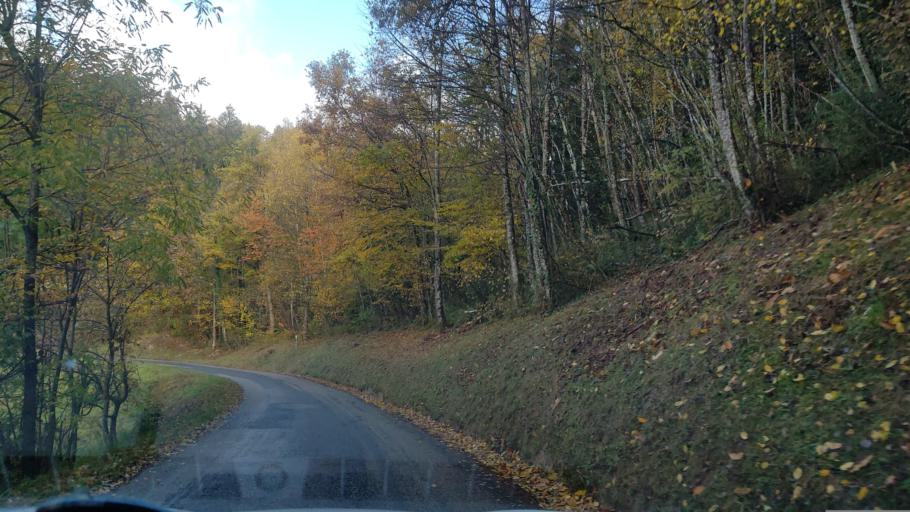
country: FR
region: Rhone-Alpes
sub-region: Departement de la Savoie
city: Novalaise
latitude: 45.6378
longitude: 5.7892
